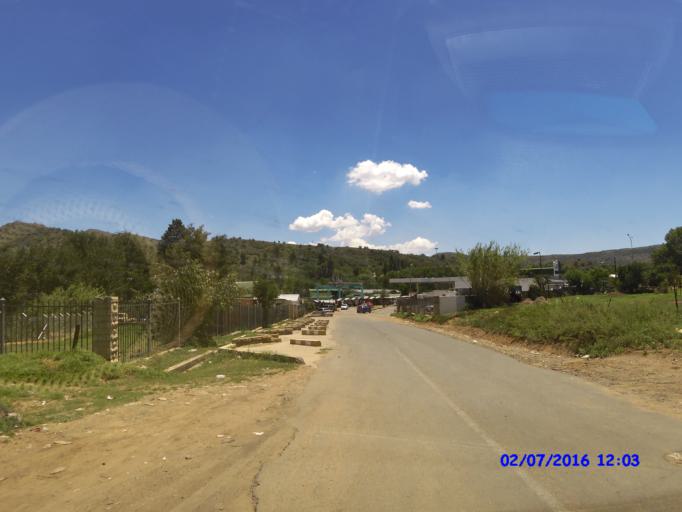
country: LS
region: Maseru
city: Maseru
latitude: -29.3010
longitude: 27.4570
